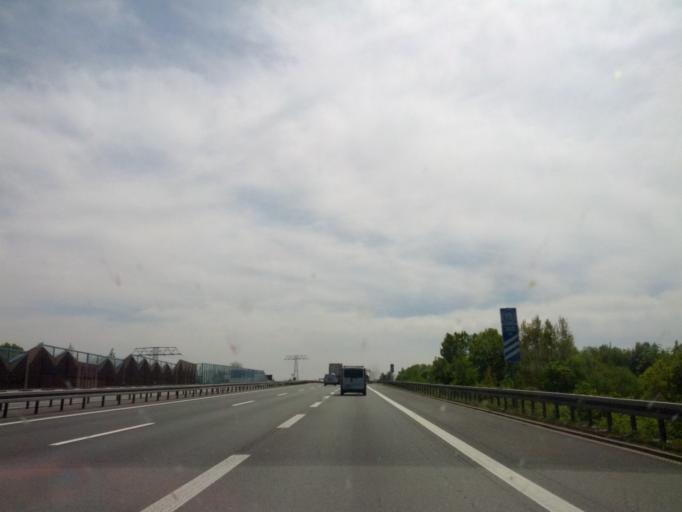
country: DE
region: Saxony
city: Neukirchen
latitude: 50.8179
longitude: 12.8565
